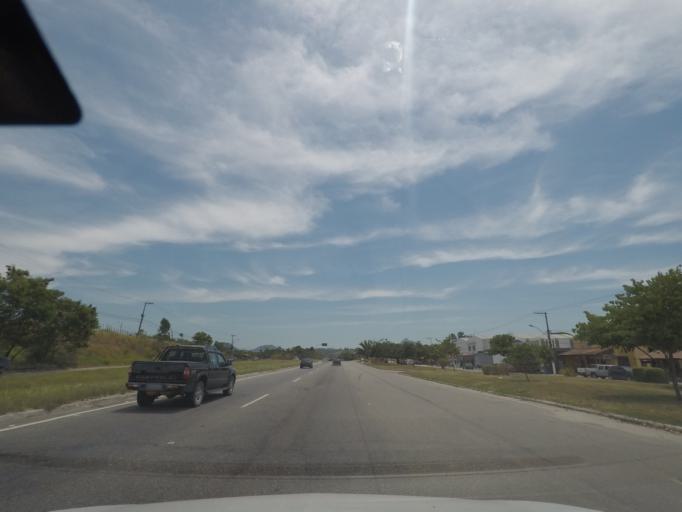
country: BR
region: Rio de Janeiro
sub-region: Marica
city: Marica
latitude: -22.9154
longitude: -42.8484
